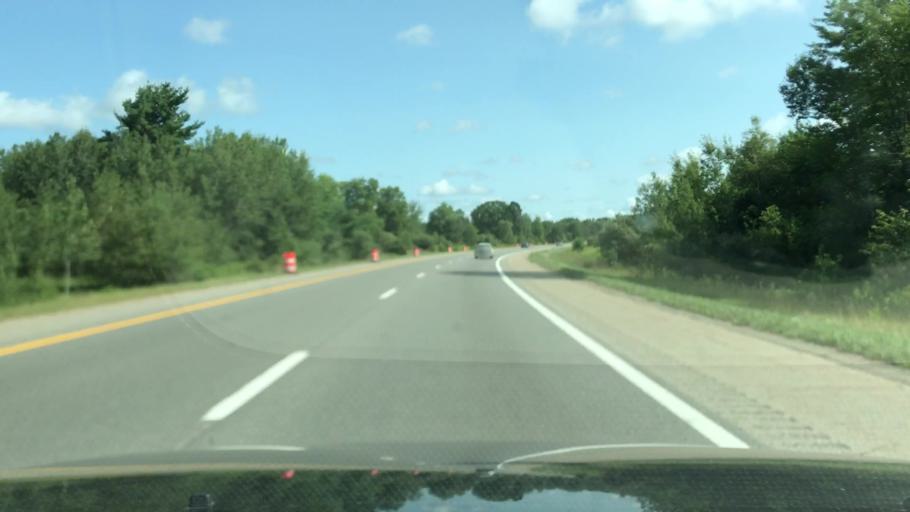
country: US
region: Michigan
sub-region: Kent County
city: Cedar Springs
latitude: 43.2495
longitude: -85.5587
